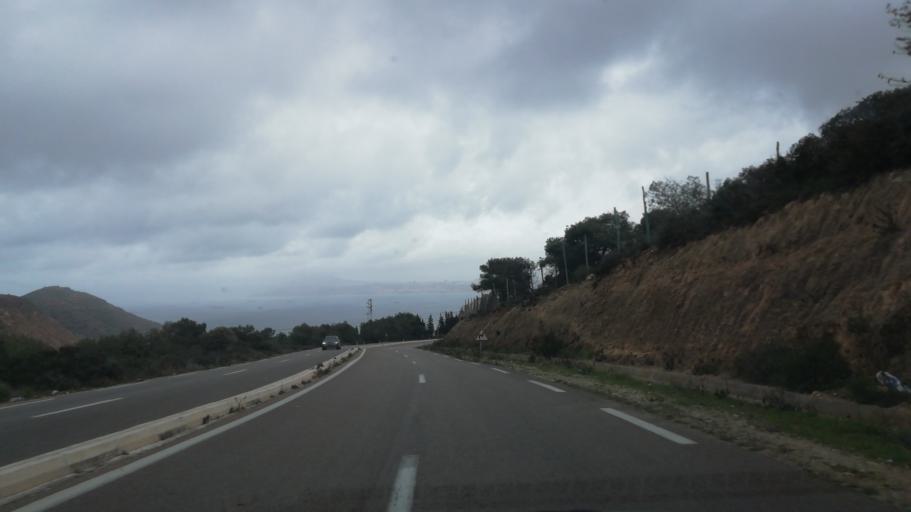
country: DZ
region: Oran
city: Mers el Kebir
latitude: 35.7196
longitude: -0.7394
